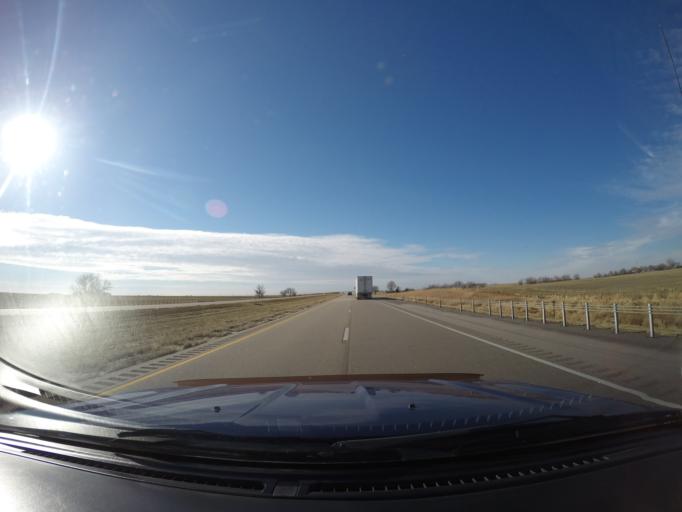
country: US
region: Nebraska
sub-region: Hamilton County
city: Aurora
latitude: 40.8222
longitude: -98.0980
